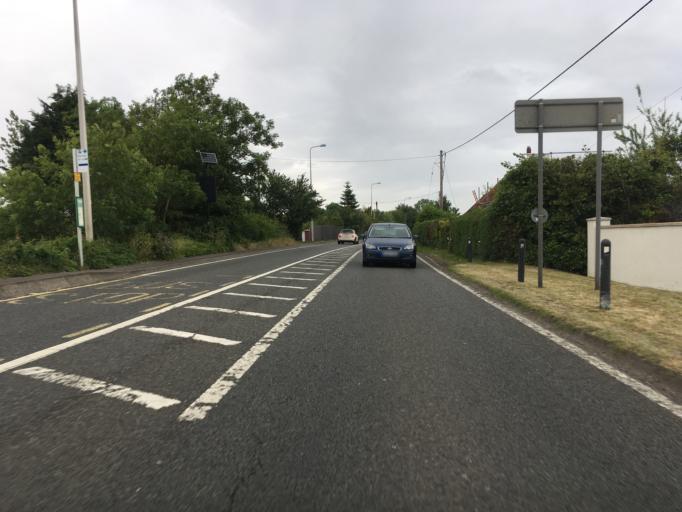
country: GB
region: England
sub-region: North Somerset
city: Kingston Seymour
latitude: 51.3724
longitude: -2.8690
